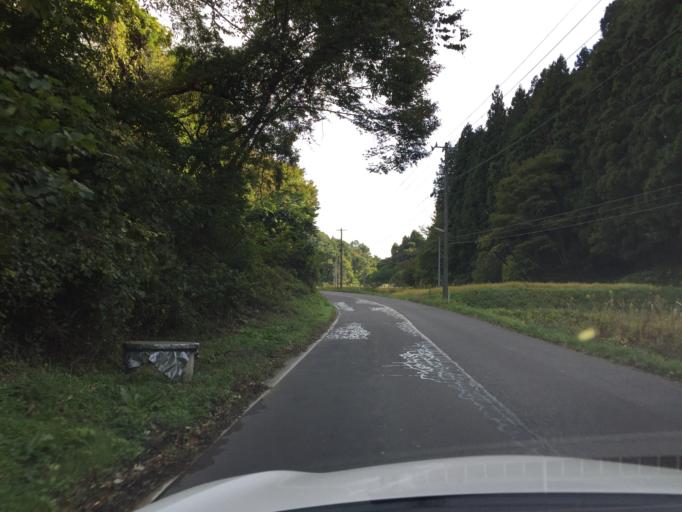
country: JP
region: Fukushima
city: Miharu
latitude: 37.3577
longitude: 140.4734
